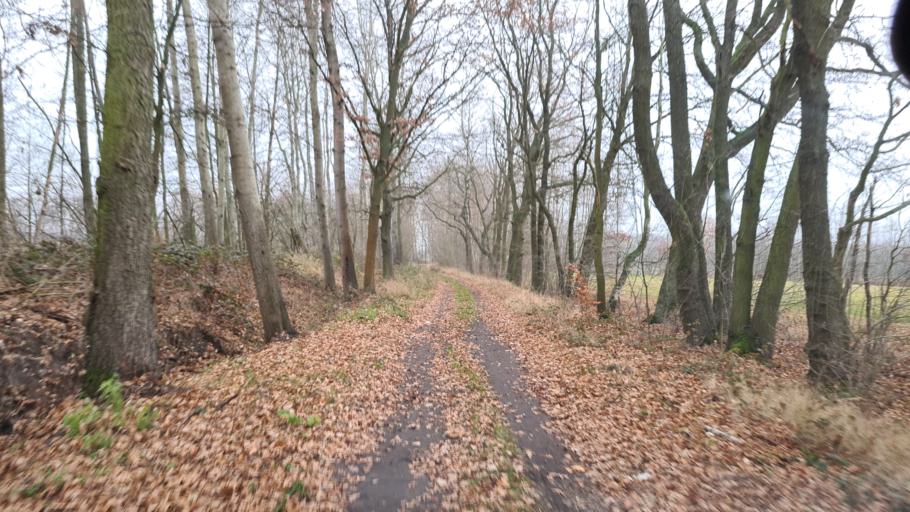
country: DE
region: Brandenburg
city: Doberlug-Kirchhain
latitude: 51.6265
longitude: 13.5321
